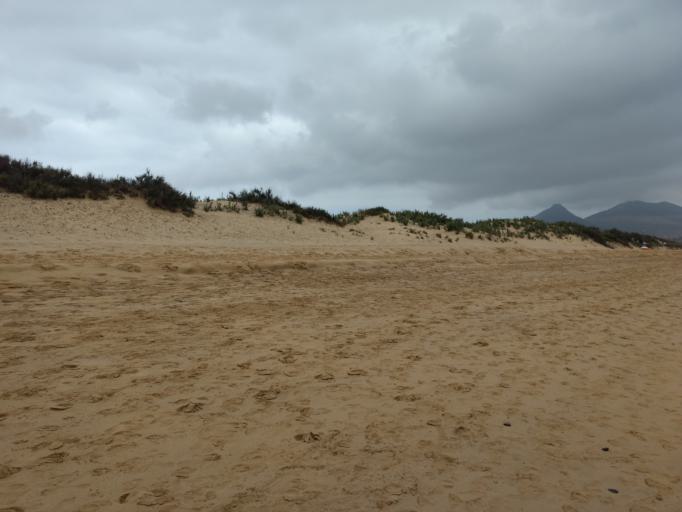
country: PT
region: Madeira
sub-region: Porto Santo
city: Vila de Porto Santo
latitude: 33.0393
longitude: -16.3564
